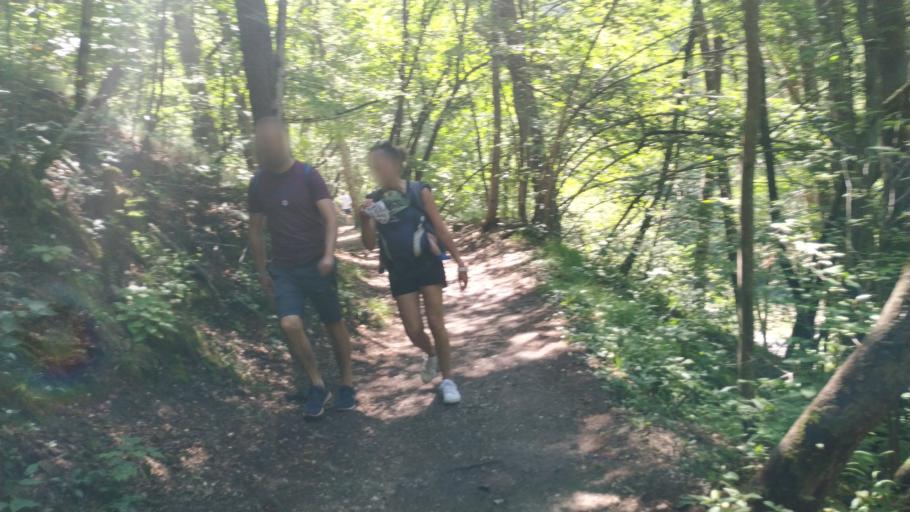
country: IT
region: Trentino-Alto Adige
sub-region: Provincia di Trento
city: Coredo
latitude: 46.3697
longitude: 11.0982
